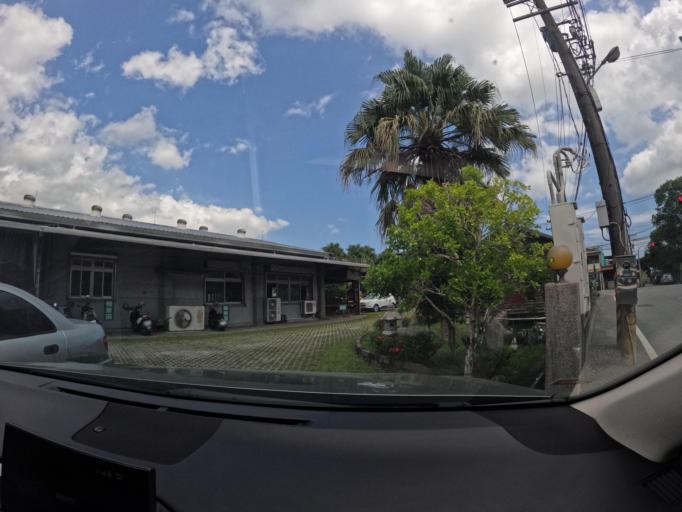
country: TW
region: Taiwan
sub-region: Hualien
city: Hualian
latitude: 23.7138
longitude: 121.4202
